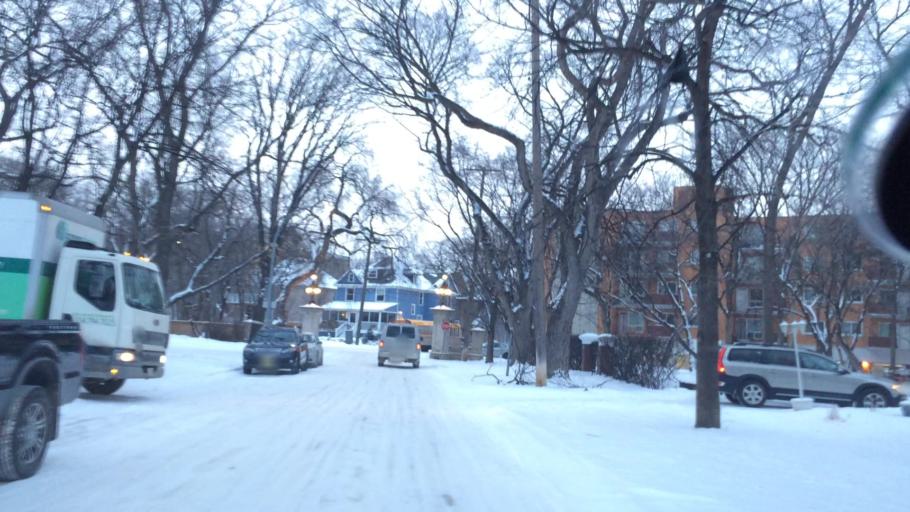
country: CA
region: Manitoba
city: Winnipeg
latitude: 49.8785
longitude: -97.1564
